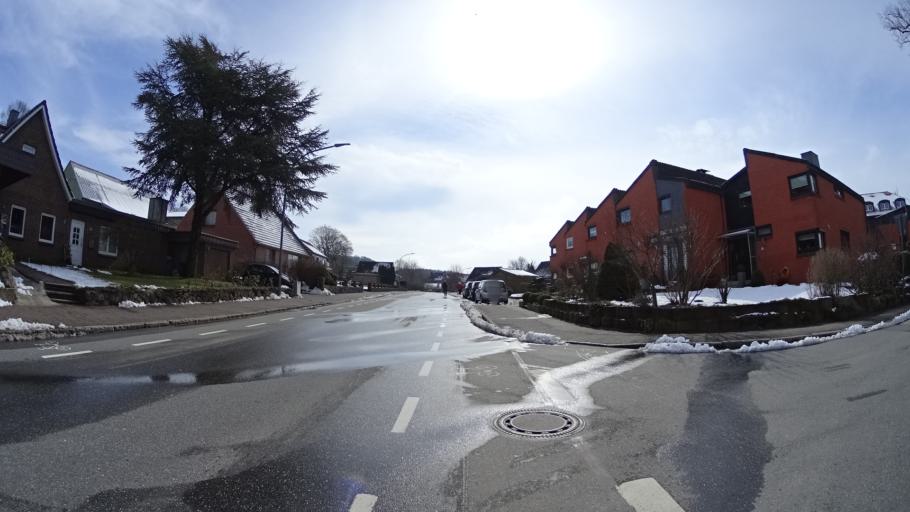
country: DE
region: Schleswig-Holstein
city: Boostedt
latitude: 54.0104
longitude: 10.0261
